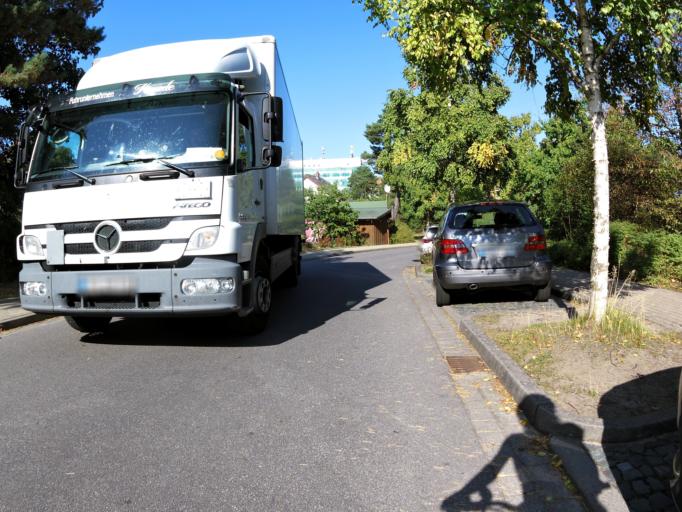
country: DE
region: Mecklenburg-Vorpommern
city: Seebad Heringsdorf
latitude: 53.9365
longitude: 14.1966
